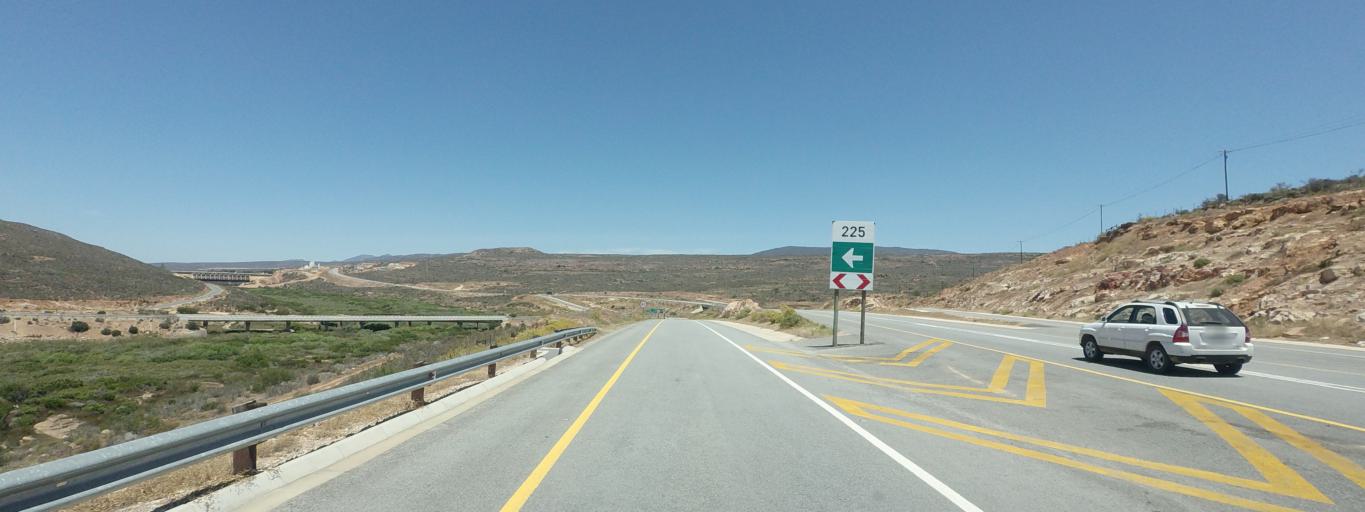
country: ZA
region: Western Cape
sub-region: West Coast District Municipality
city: Clanwilliam
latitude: -32.1698
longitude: 18.8696
